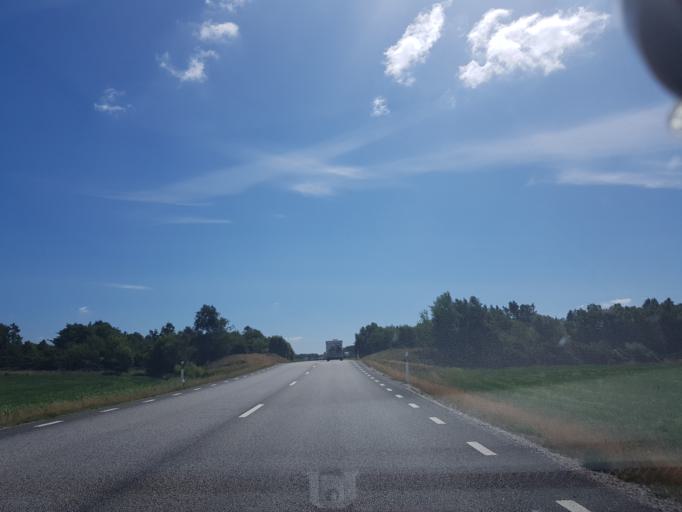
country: SE
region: Vaestra Goetaland
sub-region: Orust
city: Henan
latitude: 58.1528
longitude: 11.5727
